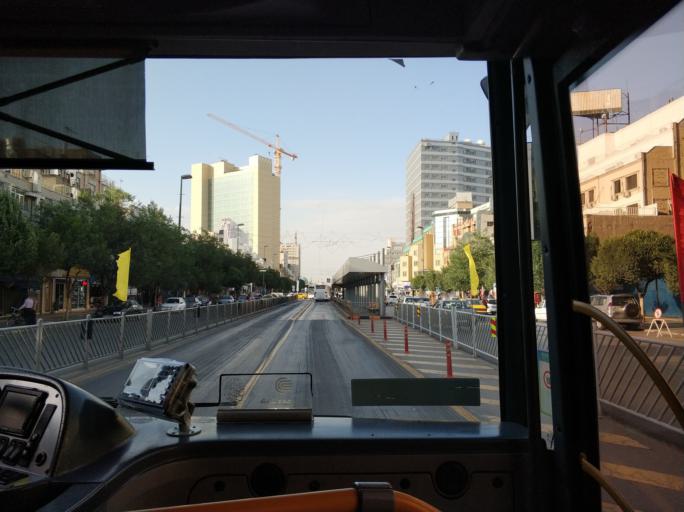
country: IR
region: Razavi Khorasan
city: Mashhad
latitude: 36.2780
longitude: 59.6072
